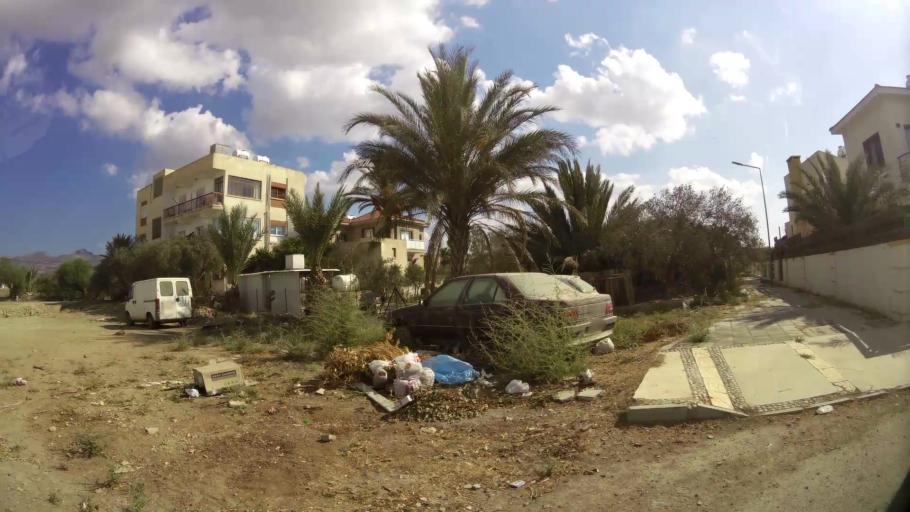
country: CY
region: Lefkosia
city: Nicosia
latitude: 35.2177
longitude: 33.3820
